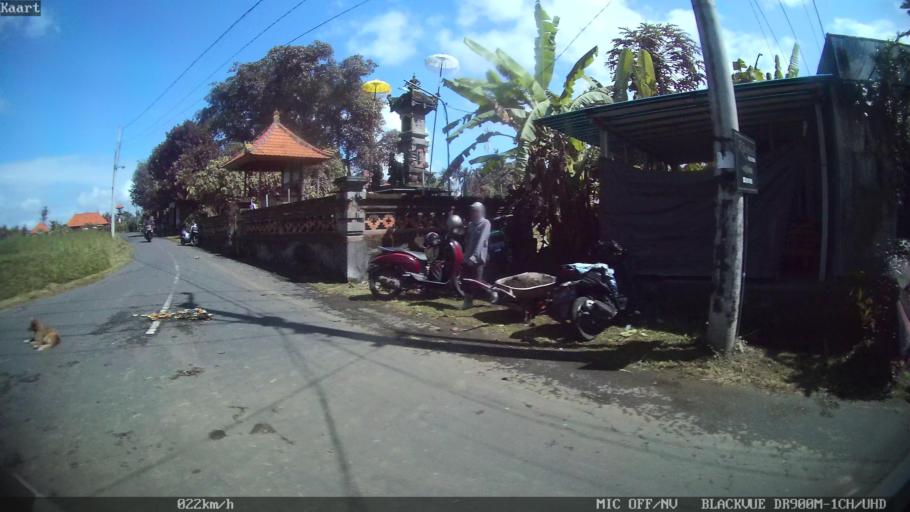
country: ID
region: Bali
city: Banjar Tebongkang
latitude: -8.5444
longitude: 115.2682
